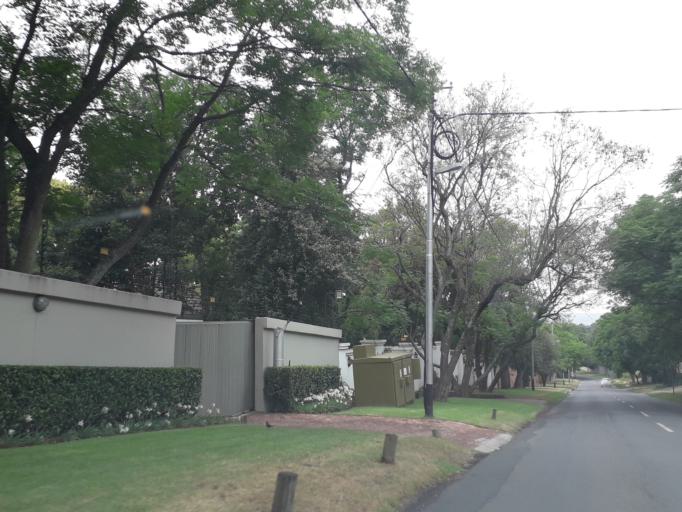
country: ZA
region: Gauteng
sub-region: City of Johannesburg Metropolitan Municipality
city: Midrand
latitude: -26.0500
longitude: 28.0379
